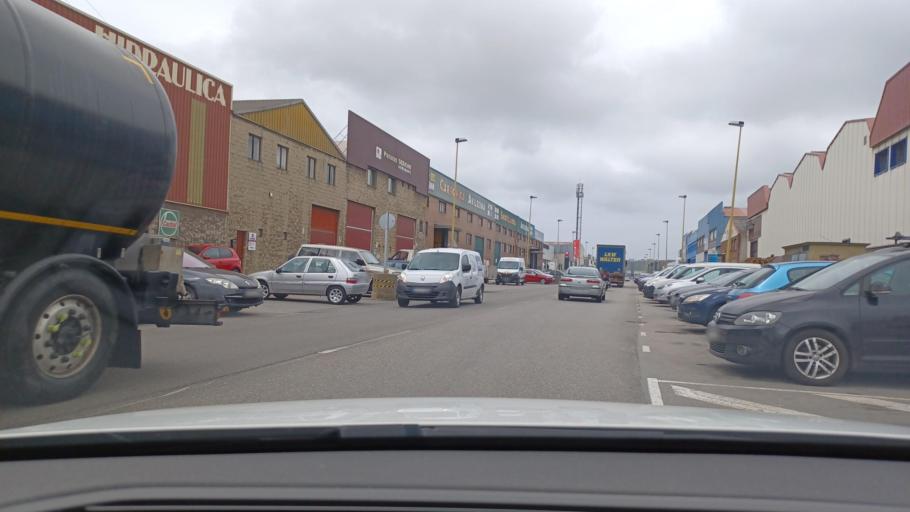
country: ES
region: Asturias
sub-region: Province of Asturias
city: Aviles
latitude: 43.5749
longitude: -5.9263
